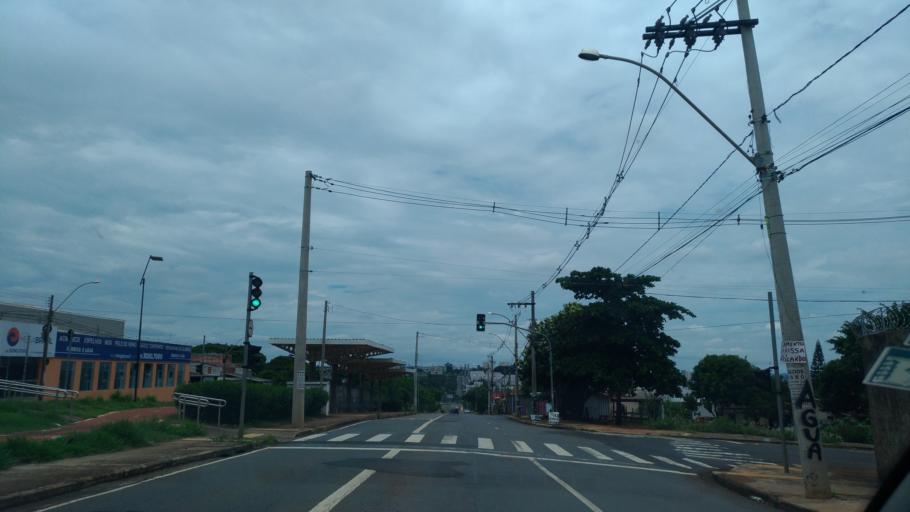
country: BR
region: Sao Paulo
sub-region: Nova Odessa
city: Nova Odessa
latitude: -22.7712
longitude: -47.3131
